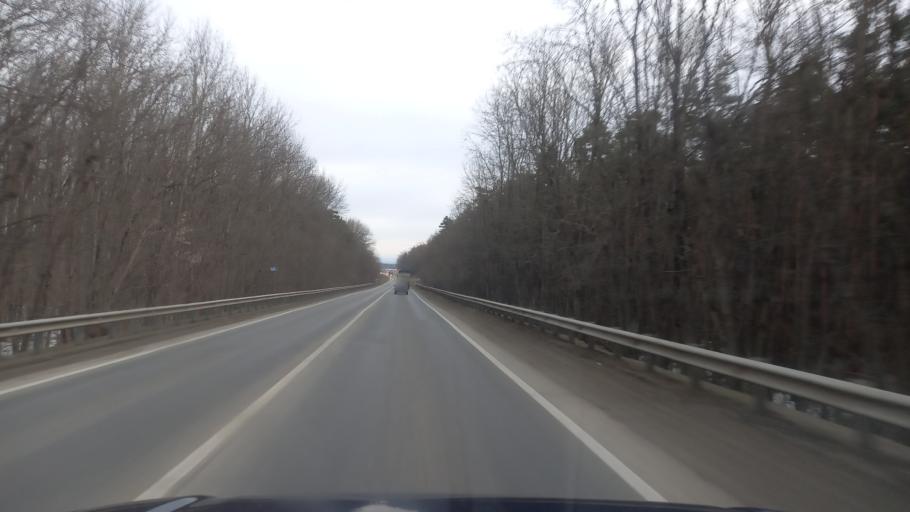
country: RU
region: Krasnodarskiy
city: Belorechensk
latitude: 44.7586
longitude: 39.9171
